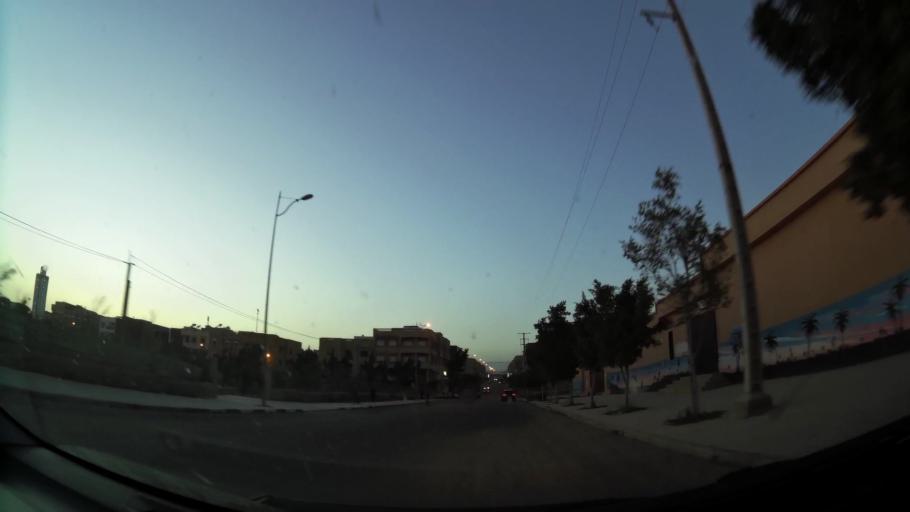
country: MA
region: Souss-Massa-Draa
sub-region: Inezgane-Ait Mellou
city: Inezgane
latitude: 30.3804
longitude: -9.4826
